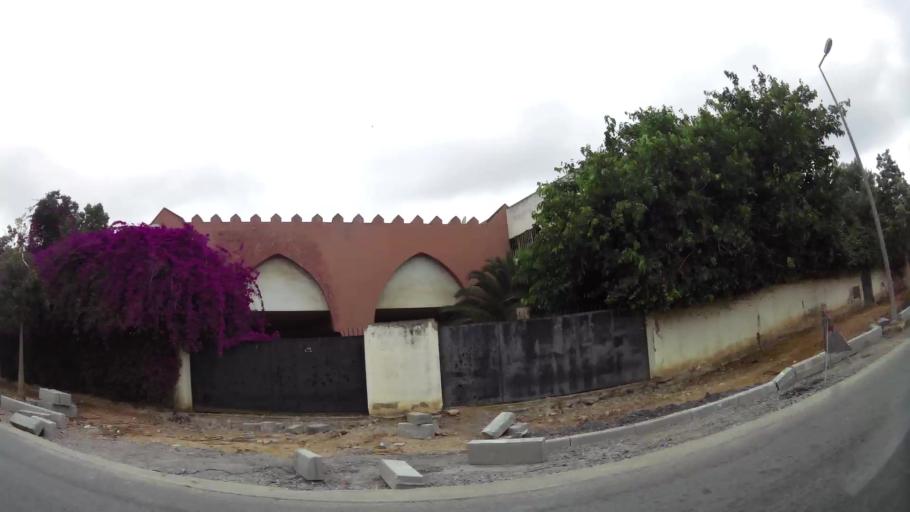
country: MA
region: Rabat-Sale-Zemmour-Zaer
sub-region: Rabat
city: Rabat
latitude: 33.9892
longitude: -6.8033
